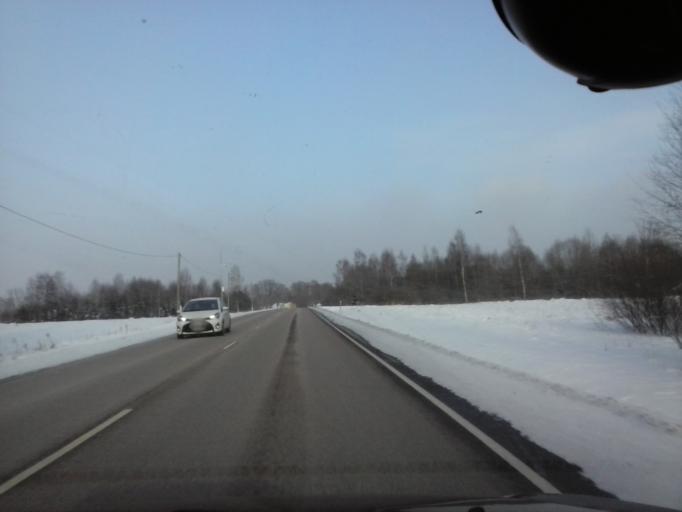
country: EE
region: Jogevamaa
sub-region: Poltsamaa linn
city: Poltsamaa
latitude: 58.4161
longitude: 26.0242
